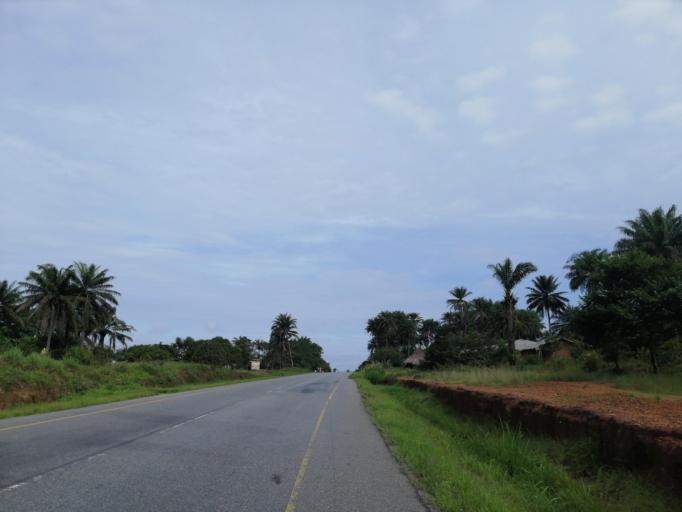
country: SL
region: Northern Province
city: Port Loko
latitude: 8.7665
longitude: -12.8889
